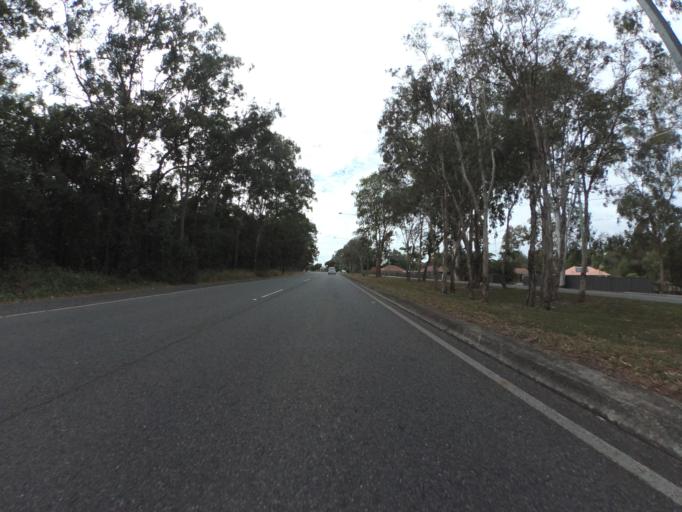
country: AU
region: Queensland
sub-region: Brisbane
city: Wynnum West
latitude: -27.4696
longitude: 153.1357
